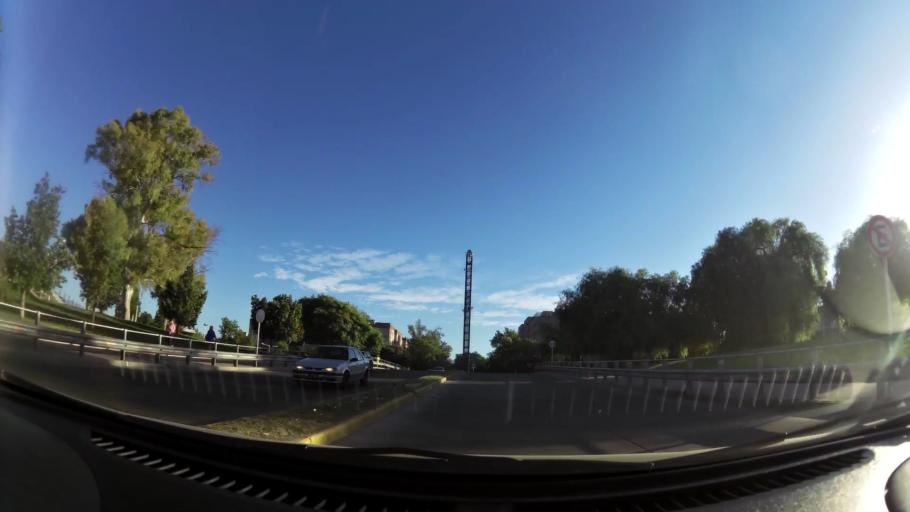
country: AR
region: Mendoza
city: Mendoza
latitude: -32.8759
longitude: -68.8408
